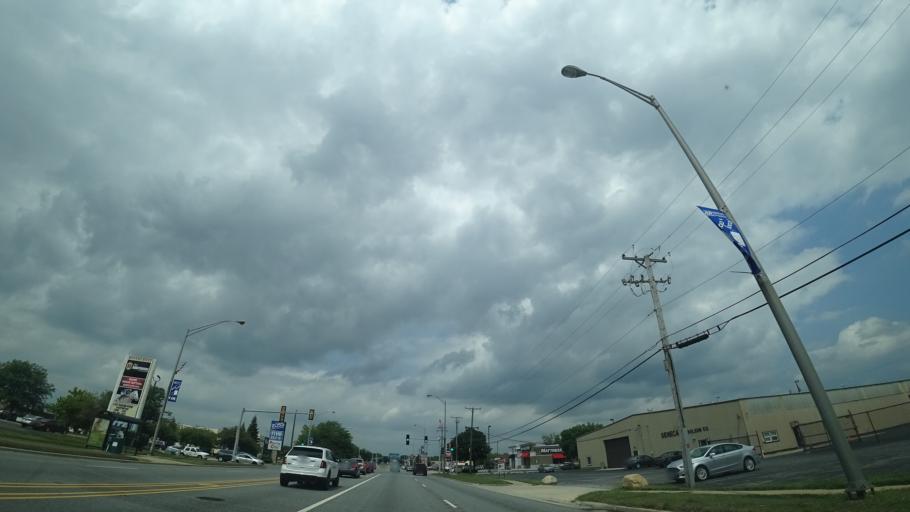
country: US
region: Illinois
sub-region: Cook County
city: Crestwood
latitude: 41.6502
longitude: -87.7381
